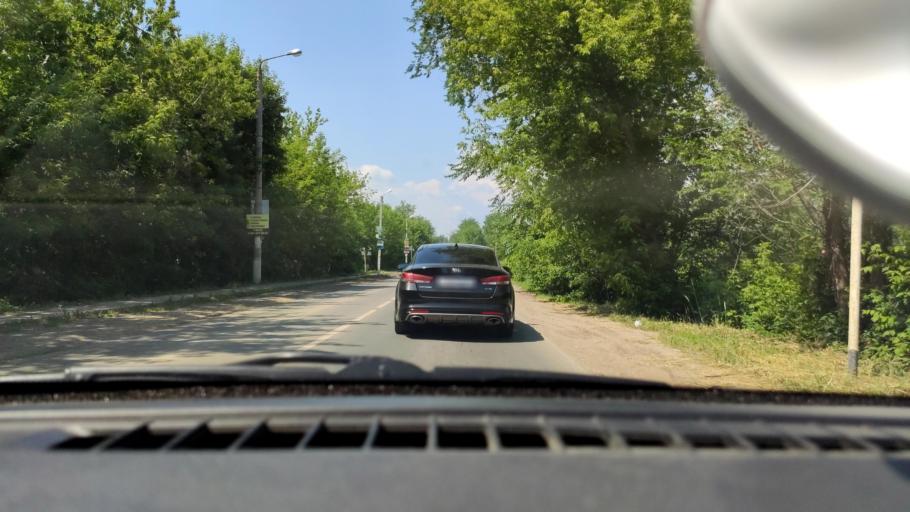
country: RU
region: Samara
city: Novokuybyshevsk
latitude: 53.1430
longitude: 49.9856
